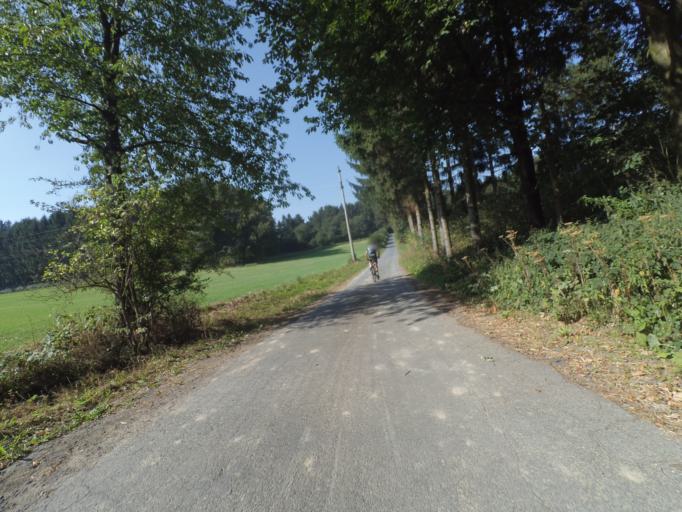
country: DE
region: North Rhine-Westphalia
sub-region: Regierungsbezirk Munster
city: Horstmar
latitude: 52.1010
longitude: 7.2859
